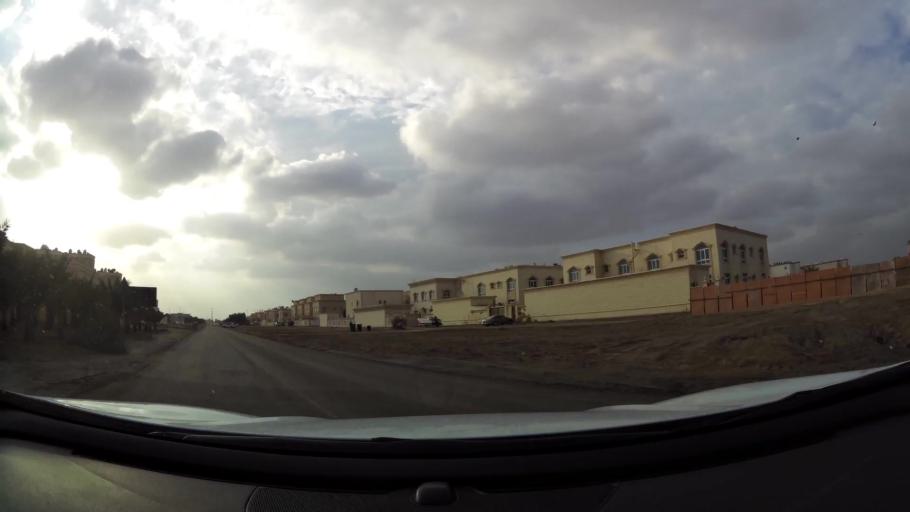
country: AE
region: Abu Dhabi
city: Abu Dhabi
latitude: 24.3529
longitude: 54.5561
